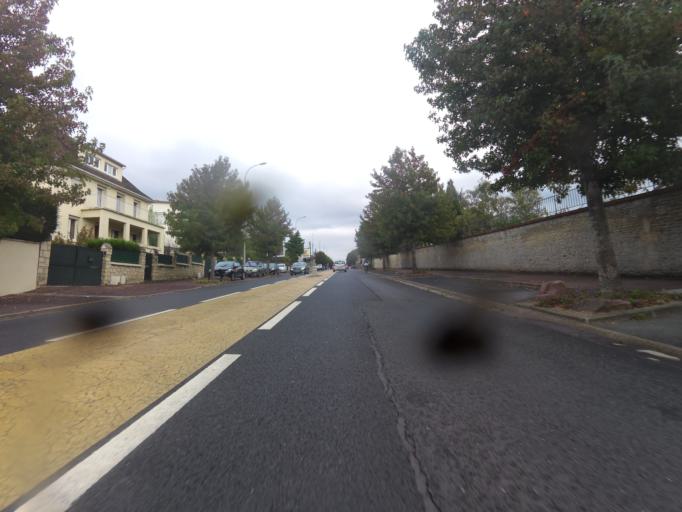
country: FR
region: Lower Normandy
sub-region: Departement du Calvados
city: Bretteville-sur-Odon
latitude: 49.1694
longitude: -0.4049
